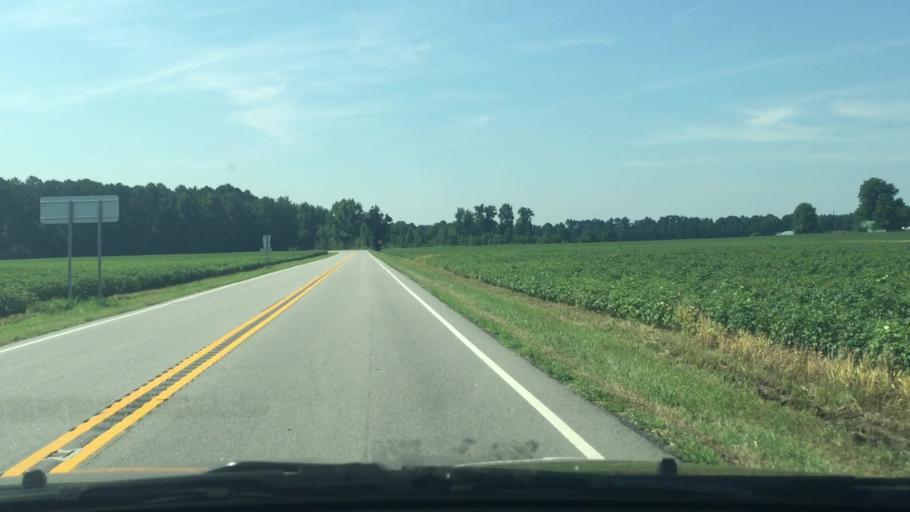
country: US
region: Virginia
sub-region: Southampton County
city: Courtland
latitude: 36.7949
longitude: -77.1292
